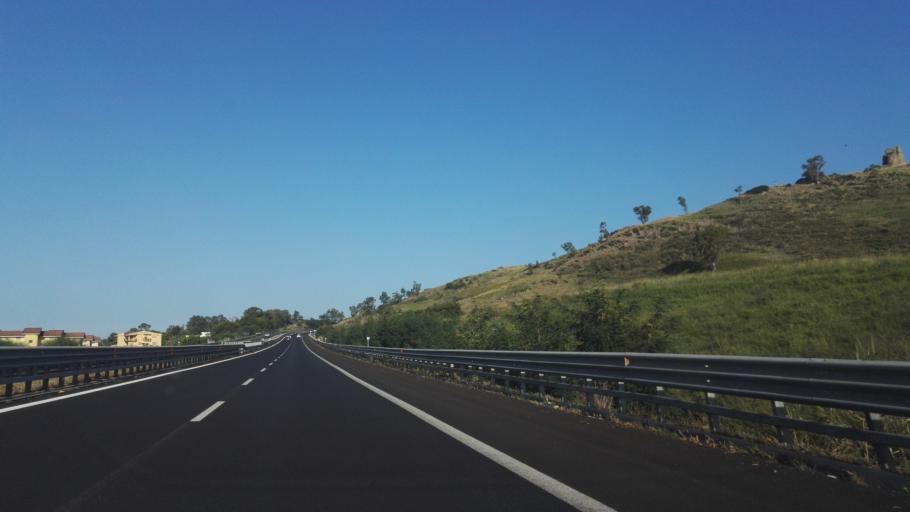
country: IT
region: Calabria
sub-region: Provincia di Catanzaro
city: Falerna Scalo
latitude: 38.9509
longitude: 16.1692
